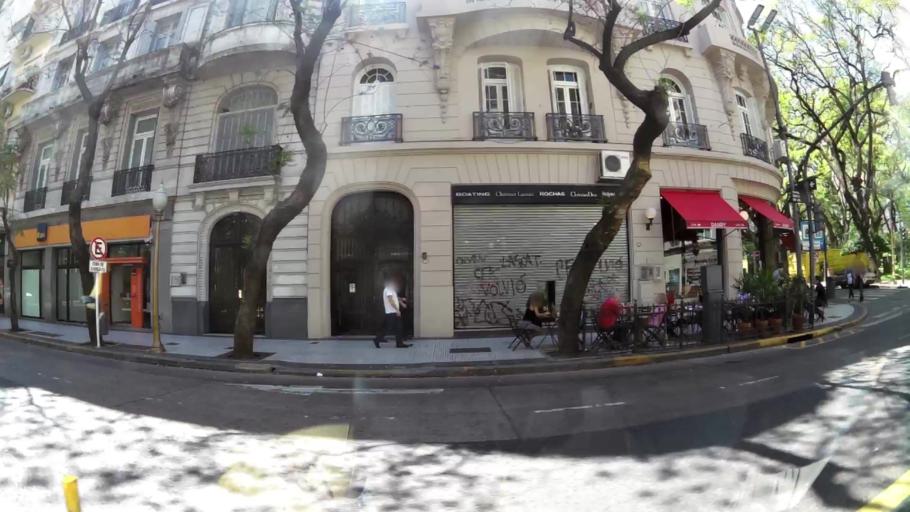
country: AR
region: Buenos Aires F.D.
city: Retiro
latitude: -34.5953
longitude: -58.3788
